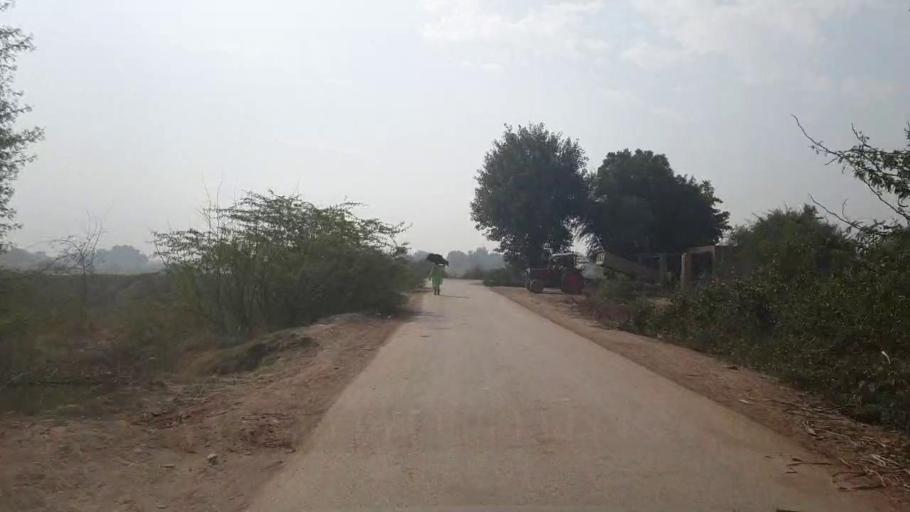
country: PK
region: Sindh
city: Hala
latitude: 25.7517
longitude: 68.4453
